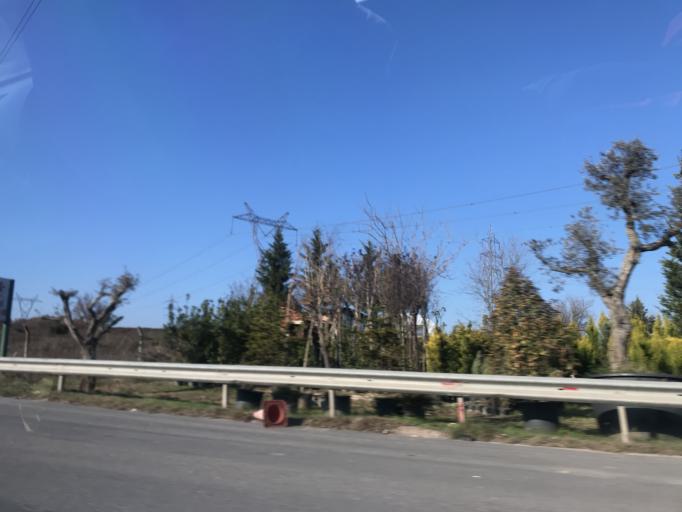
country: TR
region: Istanbul
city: Sultanbeyli
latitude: 40.9345
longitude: 29.3540
